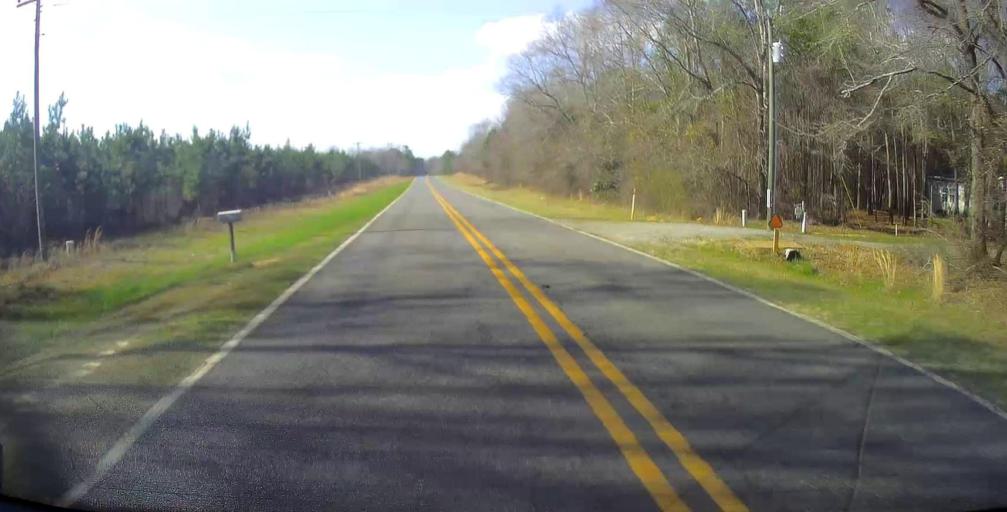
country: US
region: Georgia
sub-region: Laurens County
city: Dublin
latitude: 32.5904
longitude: -83.0636
